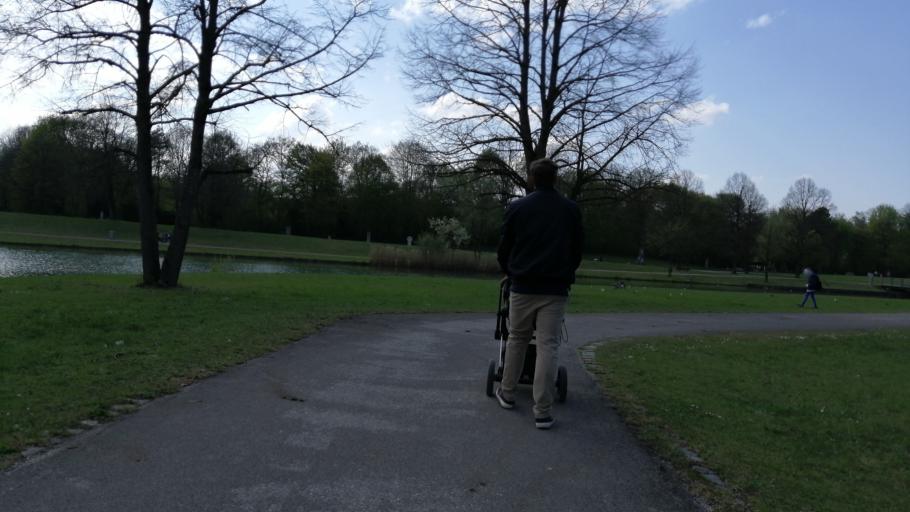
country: DE
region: Bavaria
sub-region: Upper Bavaria
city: Unterhaching
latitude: 48.0982
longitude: 11.6211
